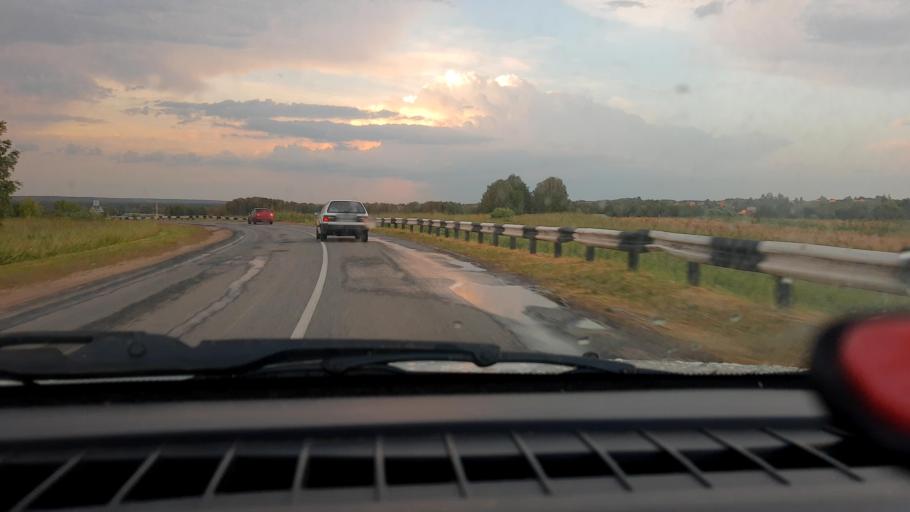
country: RU
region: Nizjnij Novgorod
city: Afonino
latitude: 56.1226
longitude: 44.0054
